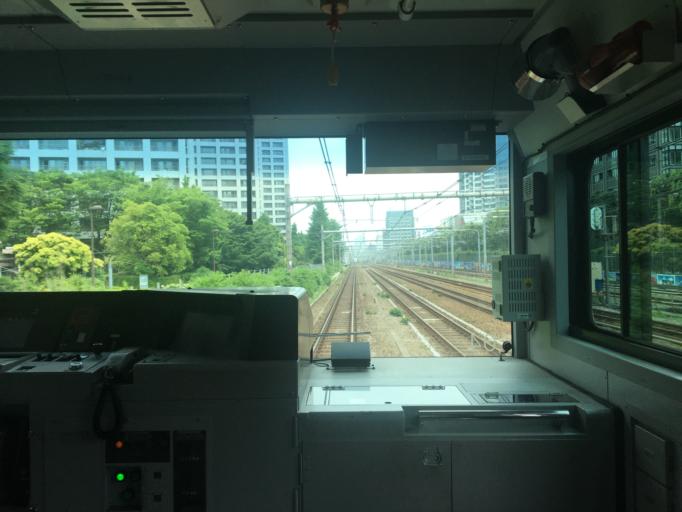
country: JP
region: Tokyo
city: Tokyo
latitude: 35.7045
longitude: 139.7007
